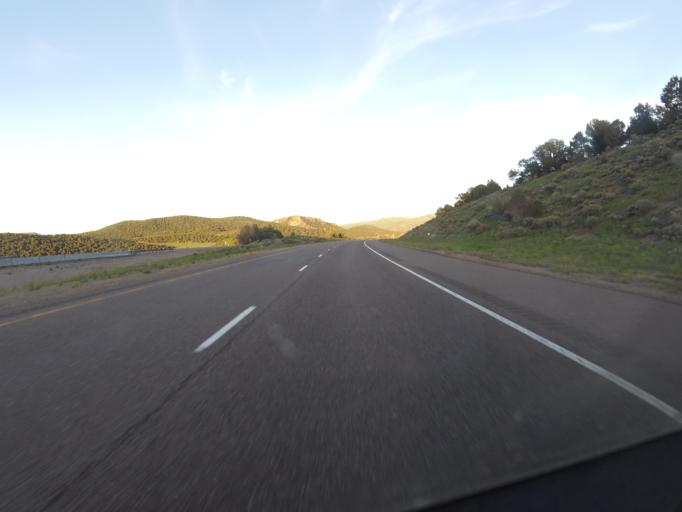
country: US
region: Utah
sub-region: Sevier County
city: Monroe
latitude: 38.5730
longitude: -112.4585
